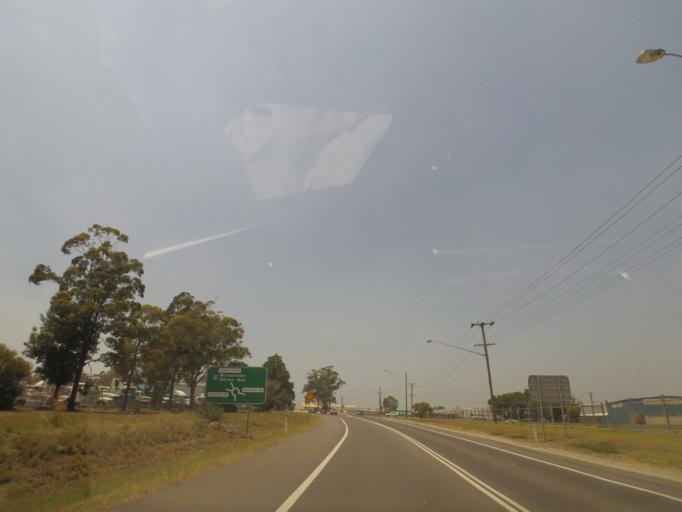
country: AU
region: New South Wales
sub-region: Newcastle
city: Beresfield
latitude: -32.8207
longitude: 151.6994
